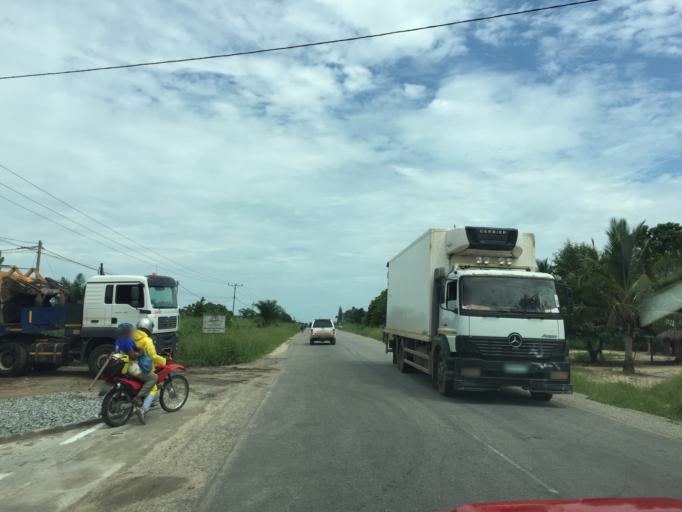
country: MZ
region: Zambezia
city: Quelimane
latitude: -17.5819
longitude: 36.8076
